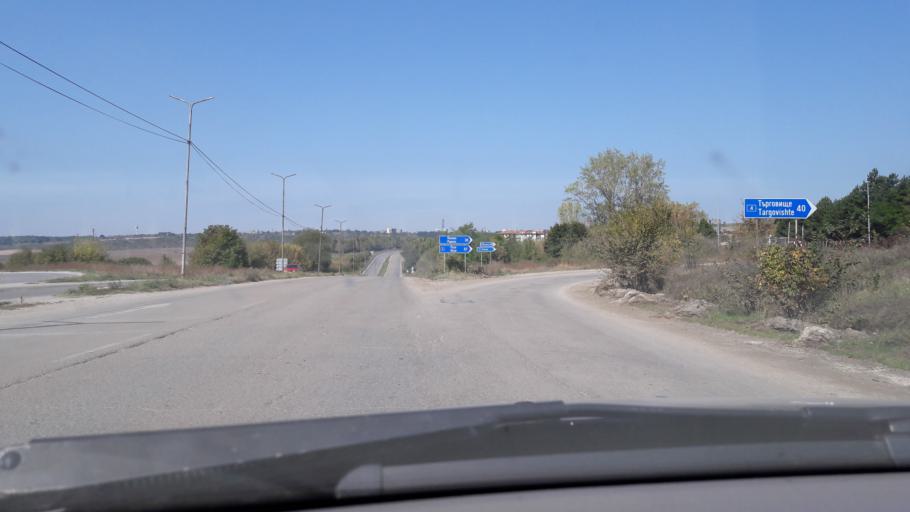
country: BG
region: Razgrad
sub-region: Obshtina Razgrad
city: Razgrad
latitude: 43.5457
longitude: 26.5121
